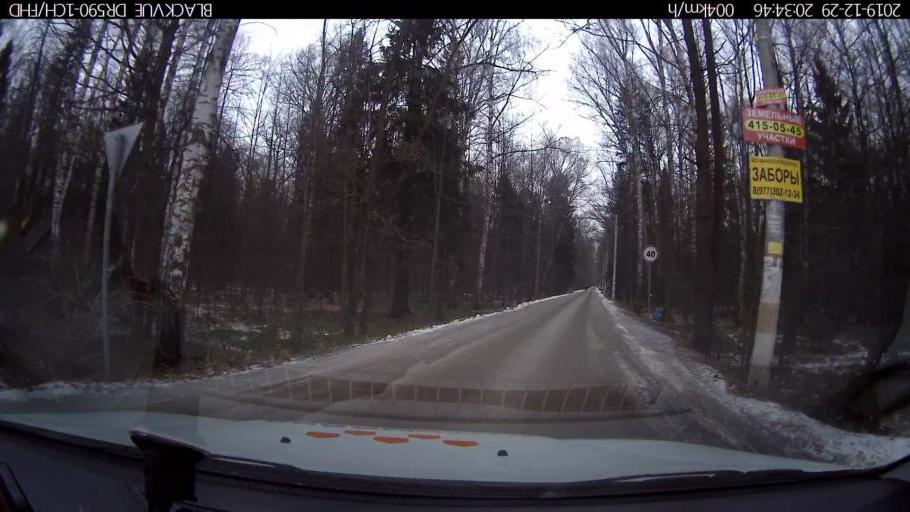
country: RU
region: Nizjnij Novgorod
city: Afonino
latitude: 56.1870
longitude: 44.0379
